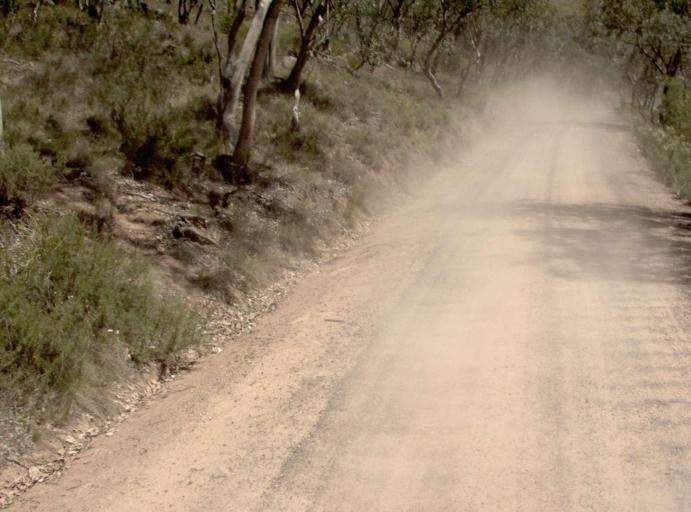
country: AU
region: New South Wales
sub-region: Snowy River
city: Jindabyne
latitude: -37.0773
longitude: 148.4915
